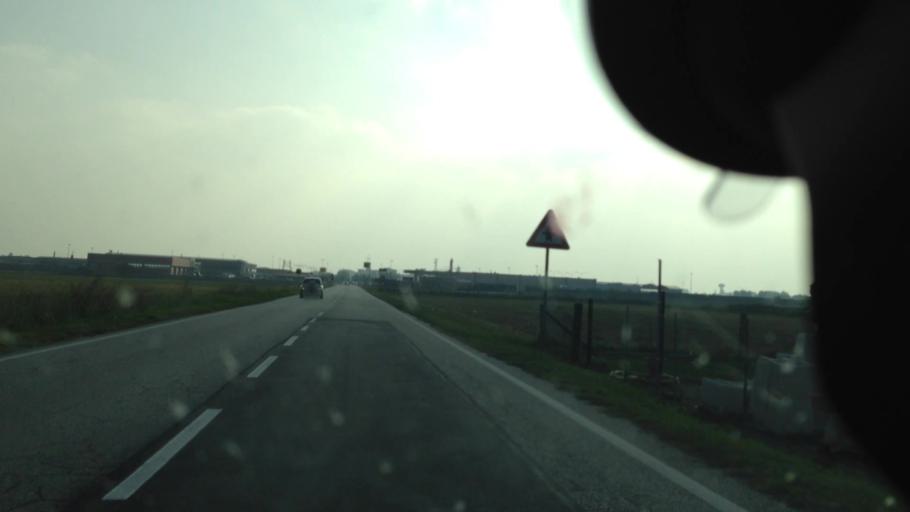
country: IT
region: Piedmont
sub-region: Provincia di Vercelli
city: Cigliano
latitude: 45.3228
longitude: 8.0335
